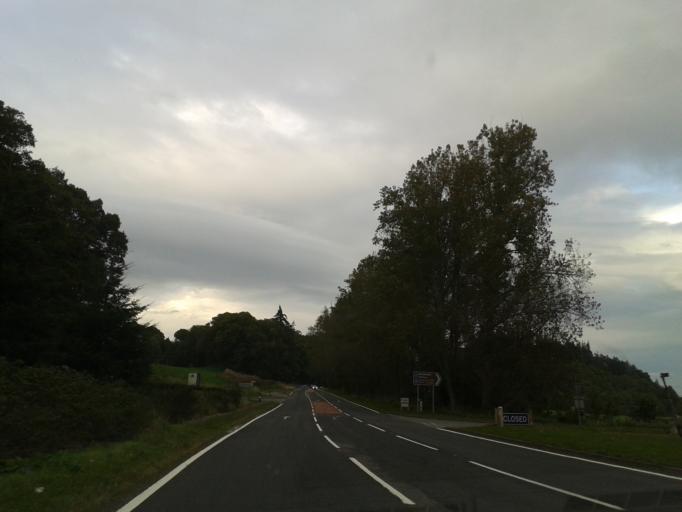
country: GB
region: Scotland
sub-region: Highland
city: Inverness
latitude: 57.4330
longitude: -4.3070
